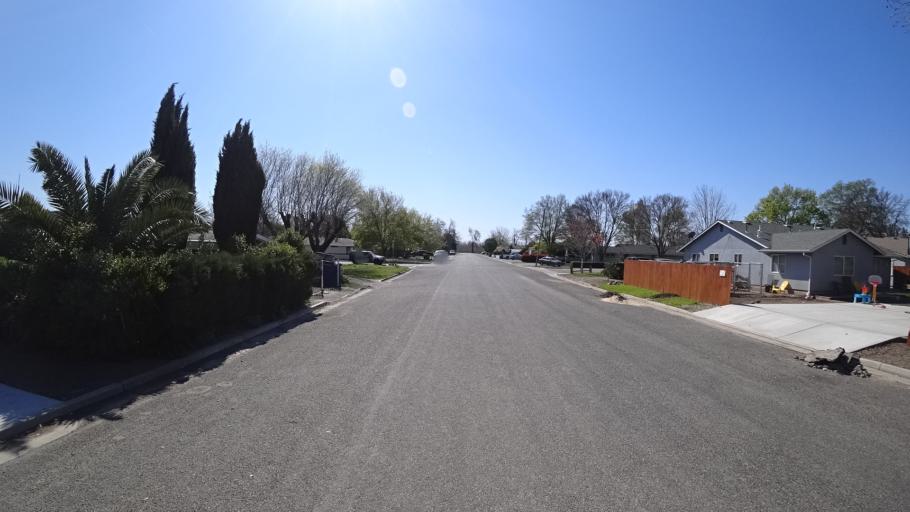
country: US
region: California
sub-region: Glenn County
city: Hamilton City
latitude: 39.7414
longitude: -122.0079
